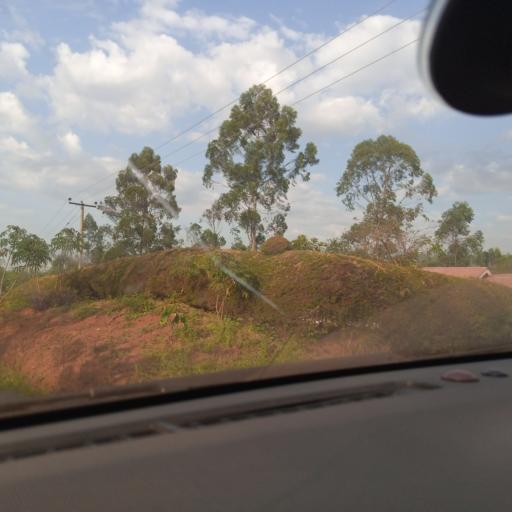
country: UG
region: Central Region
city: Masaka
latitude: -0.3493
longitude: 31.7248
